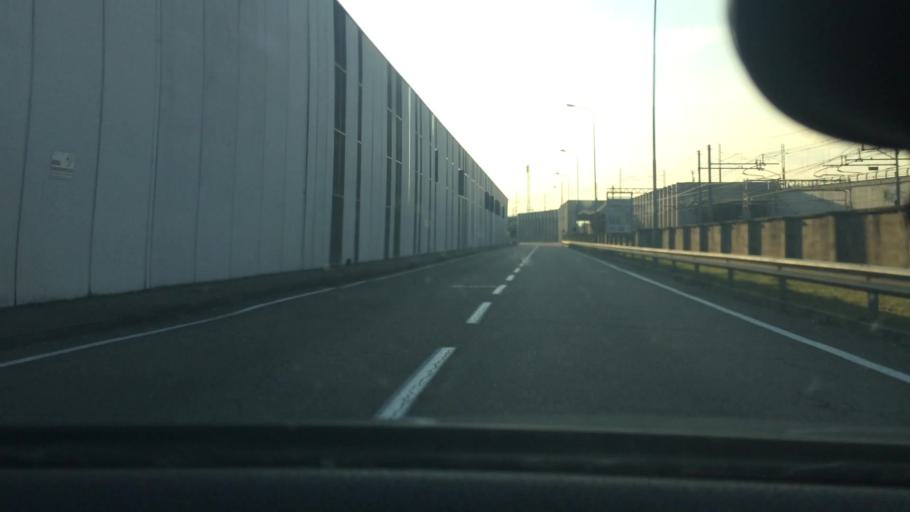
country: IT
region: Lombardy
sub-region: Citta metropolitana di Milano
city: Pero
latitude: 45.5237
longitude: 9.0793
